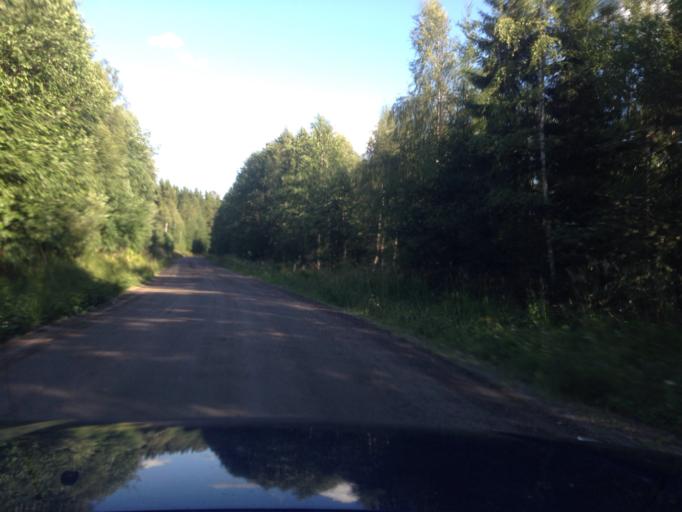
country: SE
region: Dalarna
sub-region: Ludvika Kommun
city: Abborrberget
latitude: 60.2141
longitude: 14.8671
